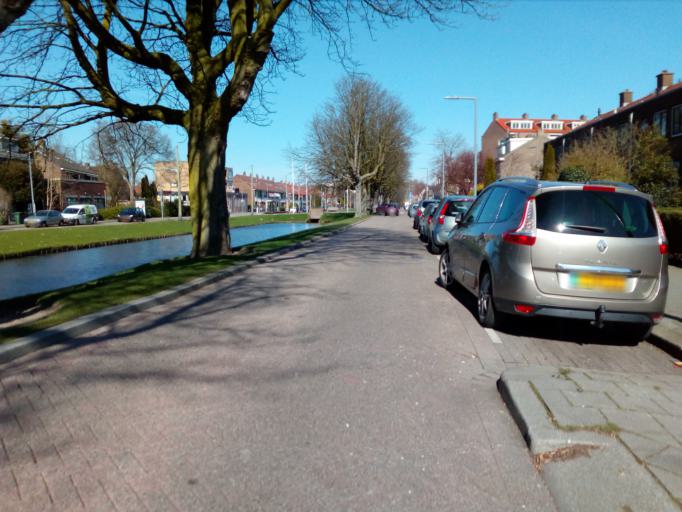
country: NL
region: South Holland
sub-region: Gemeente Lansingerland
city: Berkel en Rodenrijs
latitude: 51.9594
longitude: 4.4690
